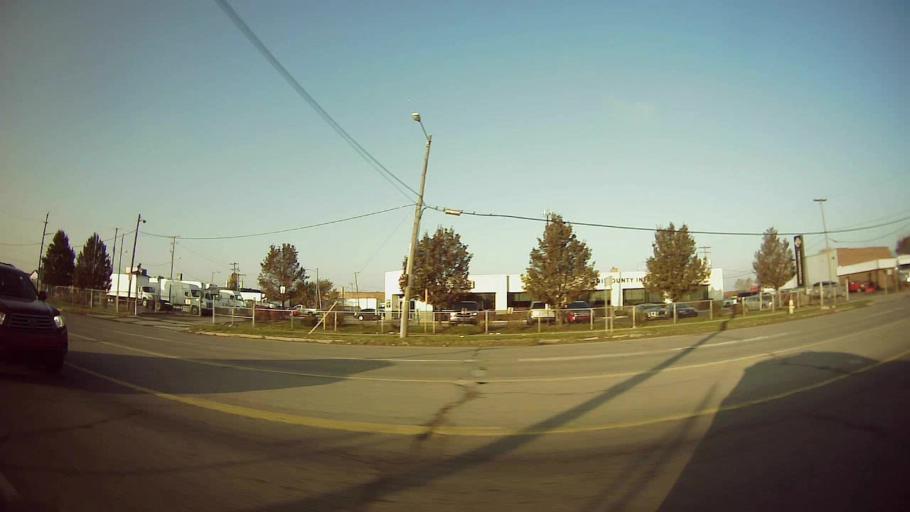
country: US
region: Michigan
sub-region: Wayne County
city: Dearborn
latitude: 42.3310
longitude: -83.1567
